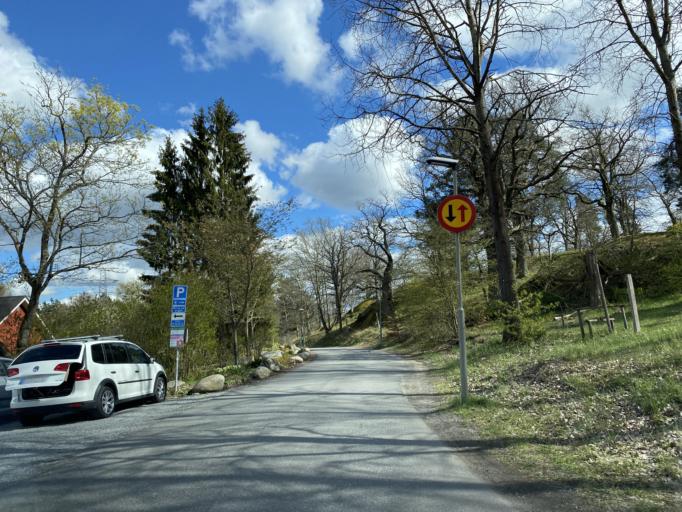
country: SE
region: Stockholm
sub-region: Stockholms Kommun
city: OEstermalm
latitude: 59.3641
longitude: 18.0712
